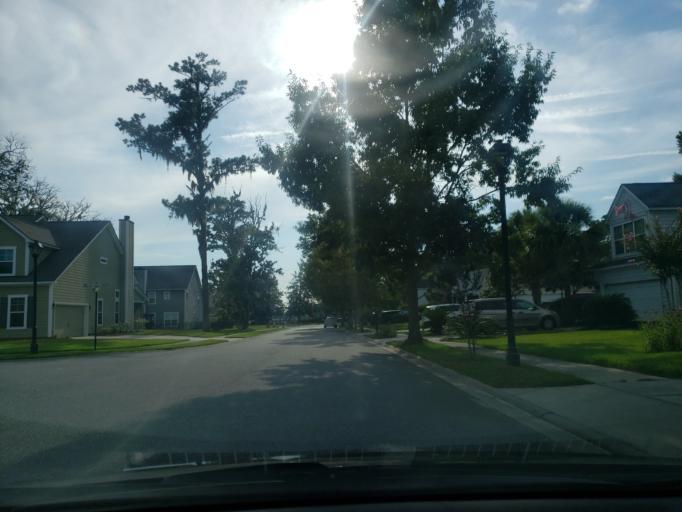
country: US
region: Georgia
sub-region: Chatham County
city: Montgomery
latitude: 31.9562
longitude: -81.1546
